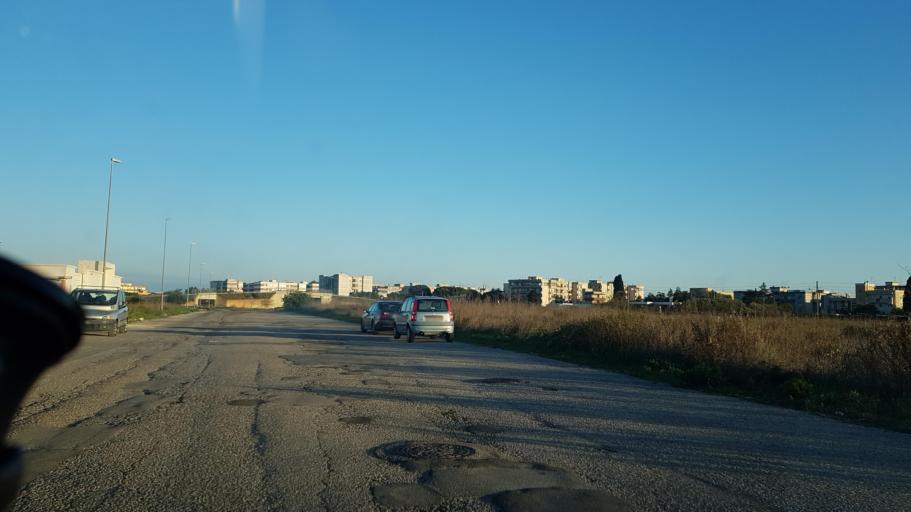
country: IT
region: Apulia
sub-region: Provincia di Brindisi
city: Mesagne
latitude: 40.5615
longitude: 17.7903
